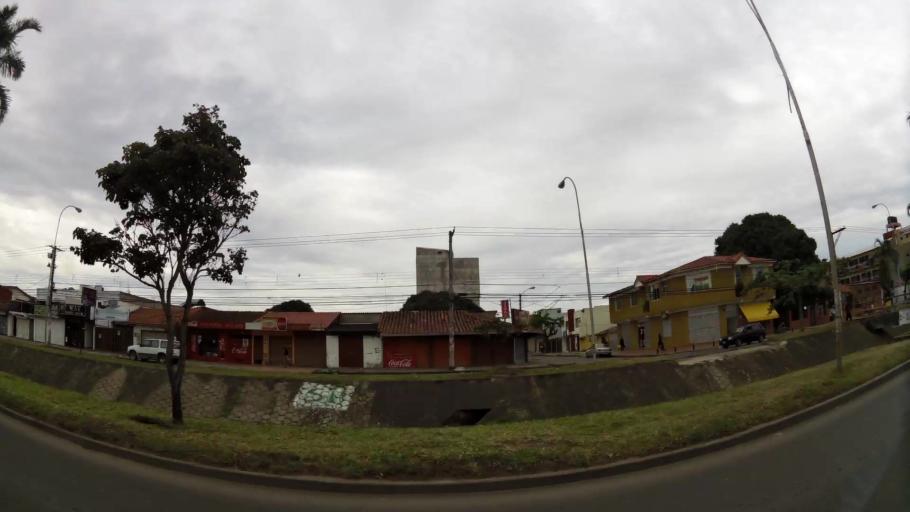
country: BO
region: Santa Cruz
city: Santa Cruz de la Sierra
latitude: -17.7816
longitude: -63.1594
